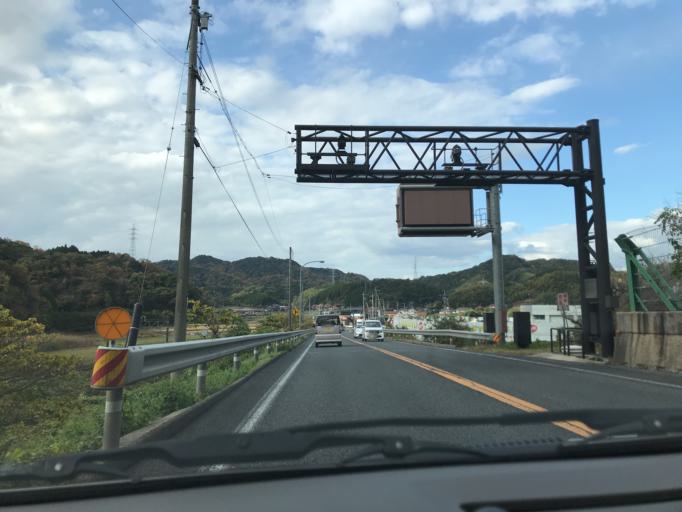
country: JP
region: Tottori
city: Yonago
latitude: 35.4082
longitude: 133.3050
